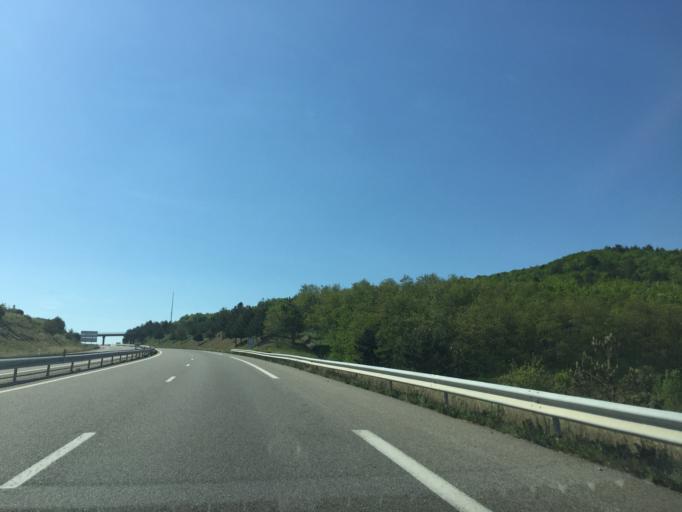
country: FR
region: Provence-Alpes-Cote d'Azur
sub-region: Departement des Alpes-de-Haute-Provence
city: Peipin
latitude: 44.1200
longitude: 5.9820
